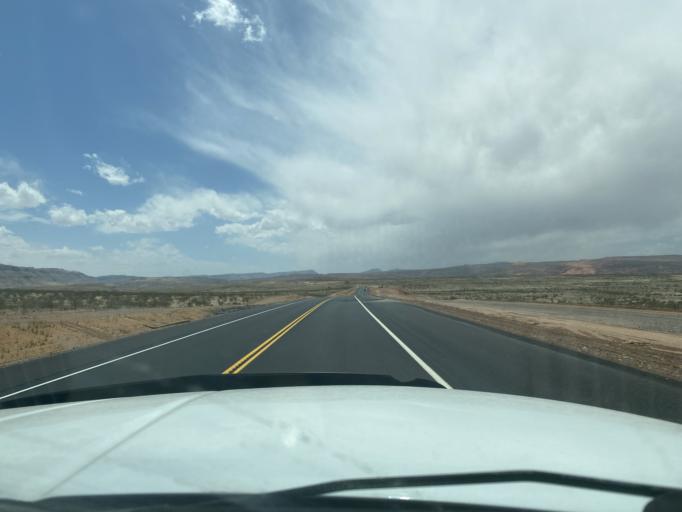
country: US
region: Utah
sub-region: Washington County
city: Hurricane
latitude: 37.1478
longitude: -113.3459
